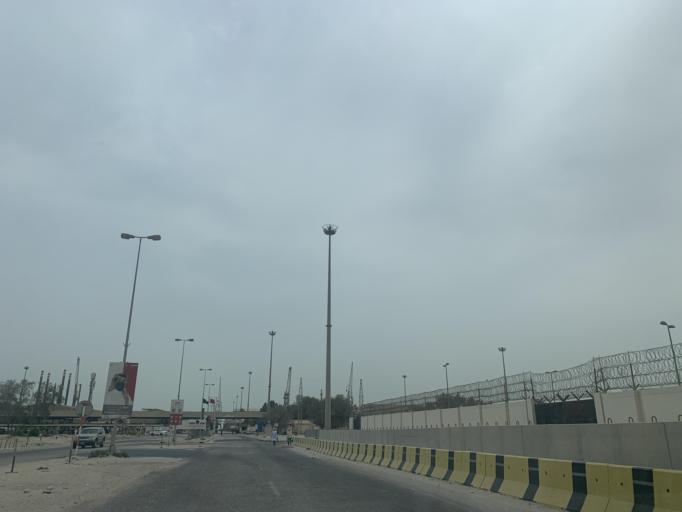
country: BH
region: Muharraq
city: Al Hadd
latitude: 26.1943
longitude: 50.6643
